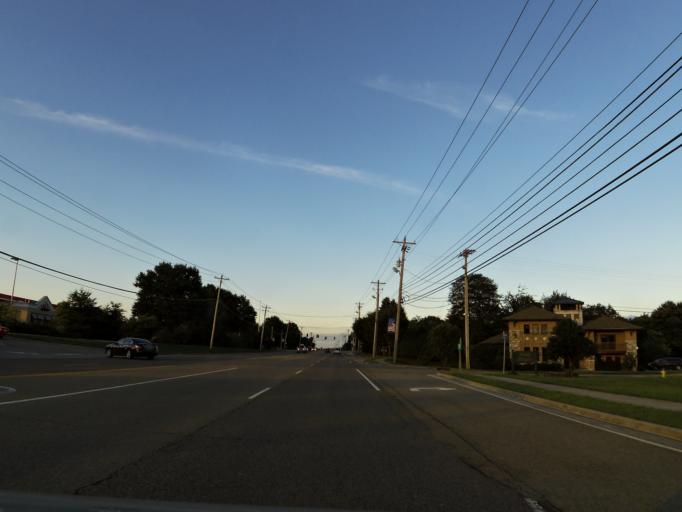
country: US
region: Tennessee
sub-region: Knox County
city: Farragut
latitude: 35.8738
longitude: -84.1771
